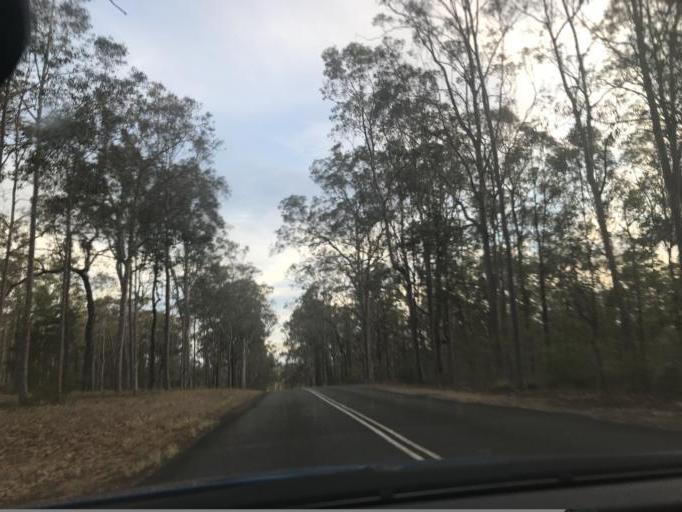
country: AU
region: New South Wales
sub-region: Cessnock
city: Cessnock
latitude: -32.8953
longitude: 151.2951
